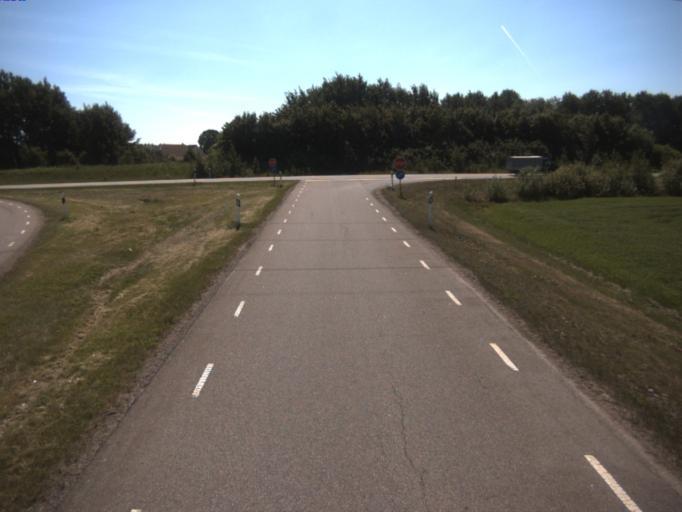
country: SE
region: Skane
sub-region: Helsingborg
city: Barslov
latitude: 56.0154
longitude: 12.8067
